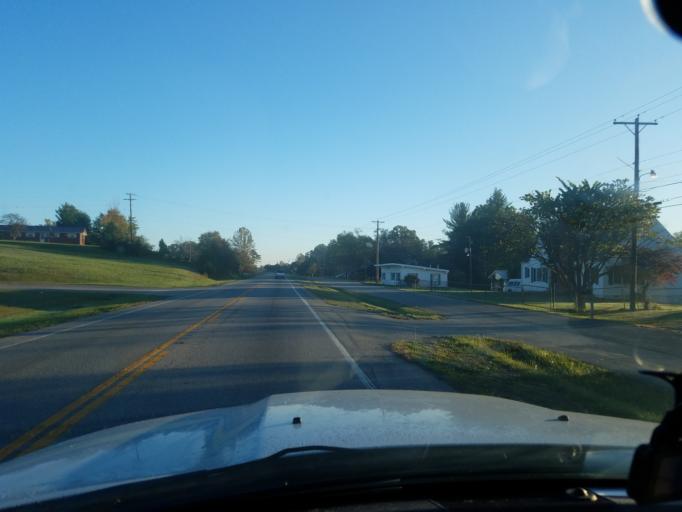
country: US
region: Kentucky
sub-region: Laurel County
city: North Corbin
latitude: 37.0257
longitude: -84.0666
